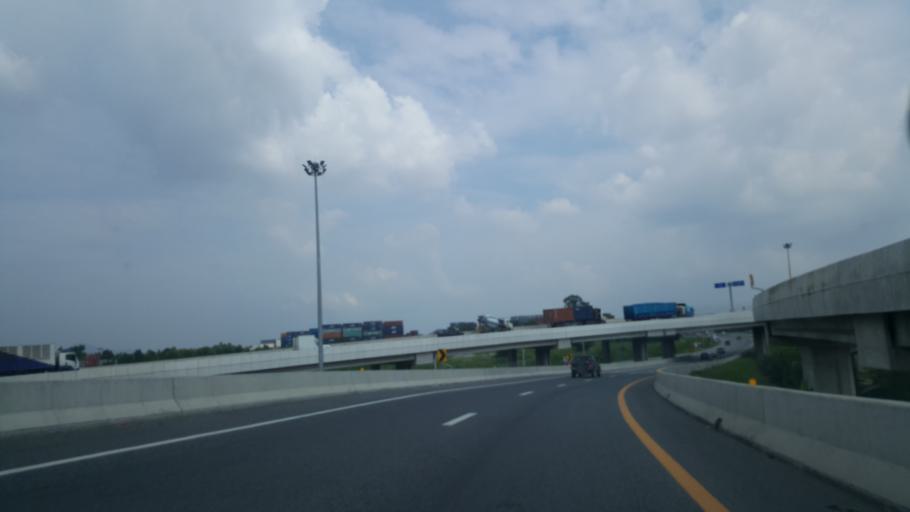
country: TH
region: Chon Buri
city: Ban Talat Bueng
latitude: 13.1177
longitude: 100.9828
